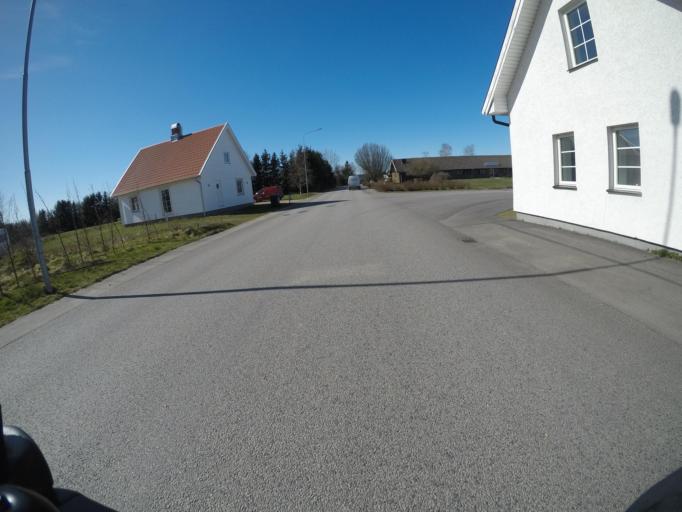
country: SE
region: Halland
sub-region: Laholms Kommun
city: Laholm
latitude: 56.4986
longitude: 13.0334
